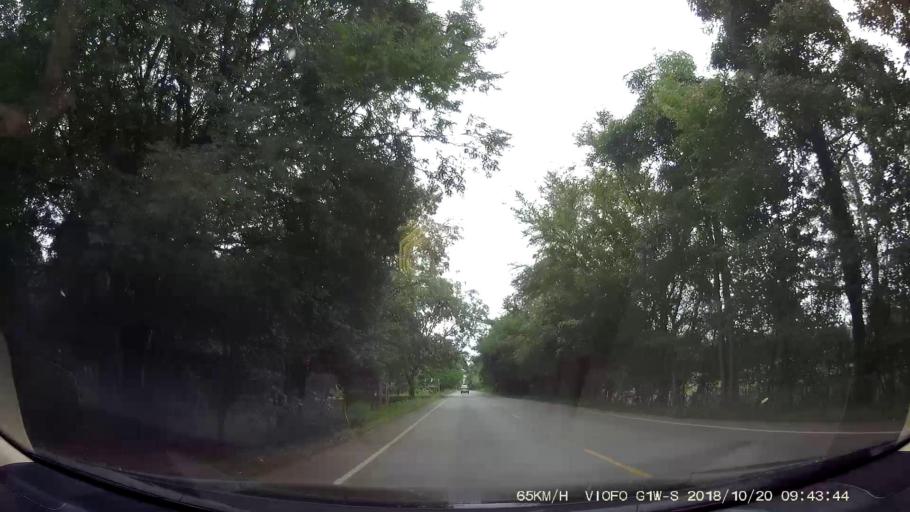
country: TH
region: Chaiyaphum
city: Khon San
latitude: 16.4763
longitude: 101.9469
